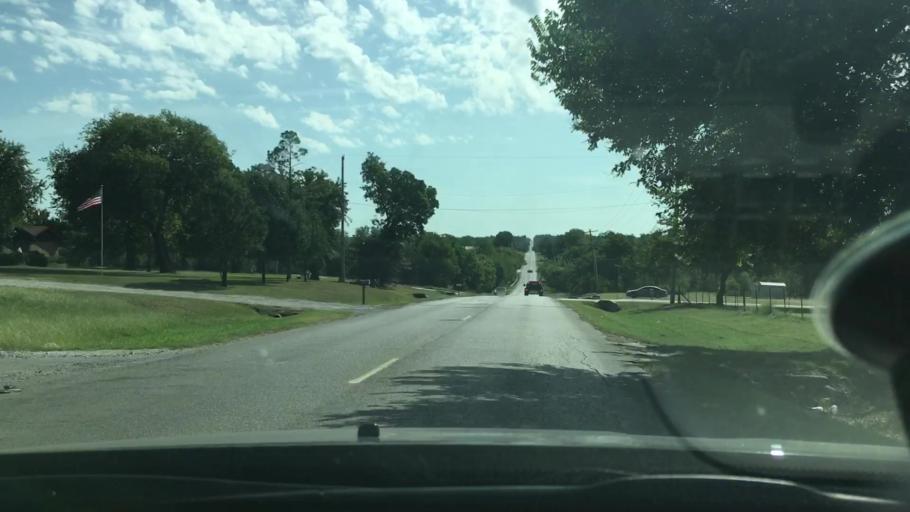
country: US
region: Oklahoma
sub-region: Carter County
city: Ardmore
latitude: 34.1583
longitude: -97.1133
